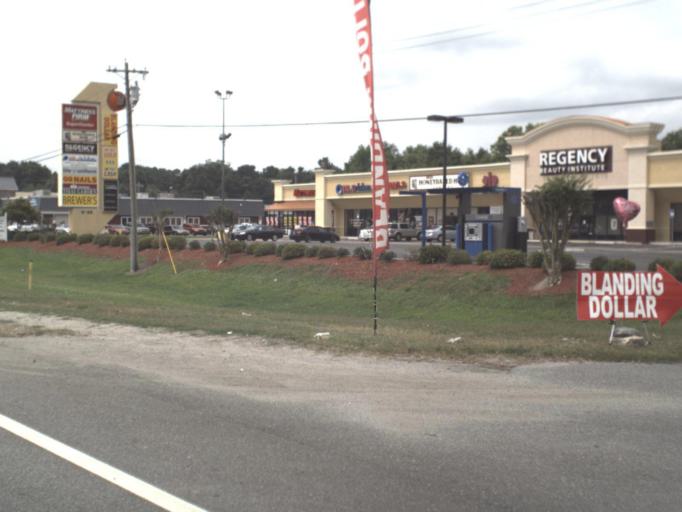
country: US
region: Florida
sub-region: Clay County
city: Bellair-Meadowbrook Terrace
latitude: 30.1892
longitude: -81.7395
